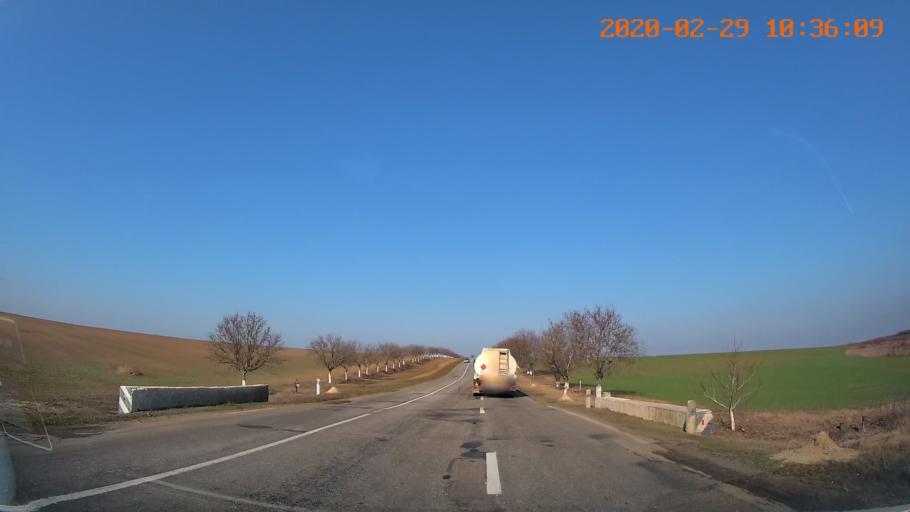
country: MD
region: Anenii Noi
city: Varnita
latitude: 46.9925
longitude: 29.5100
